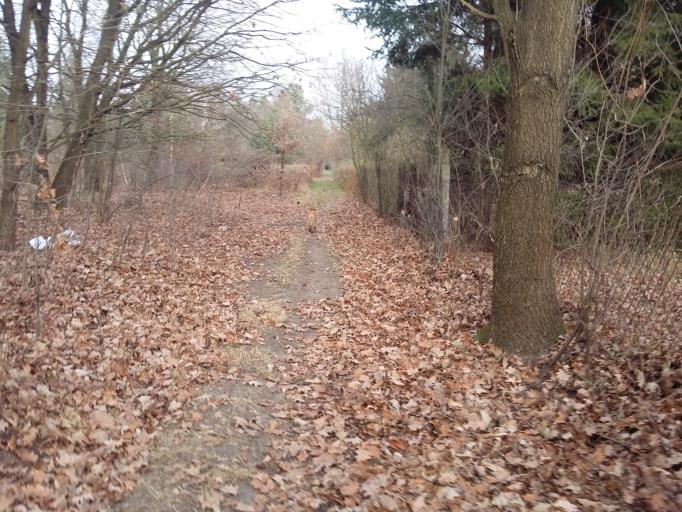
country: PL
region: Lodz Voivodeship
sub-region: Powiat pabianicki
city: Ksawerow
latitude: 51.7326
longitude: 19.4116
